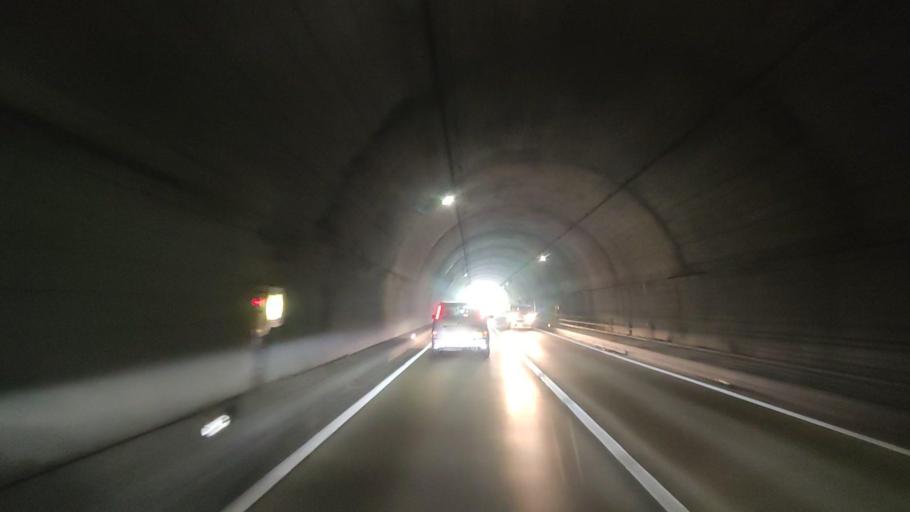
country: JP
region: Gifu
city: Godo
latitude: 35.5075
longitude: 136.6645
